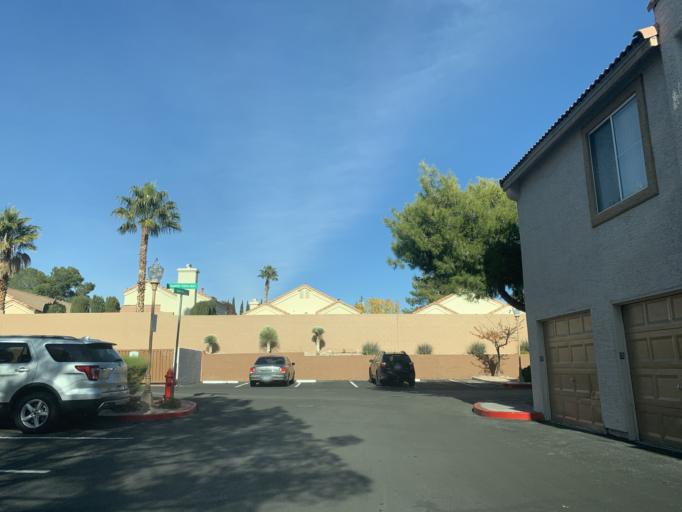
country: US
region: Nevada
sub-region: Clark County
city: Summerlin South
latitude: 36.1309
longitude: -115.2911
